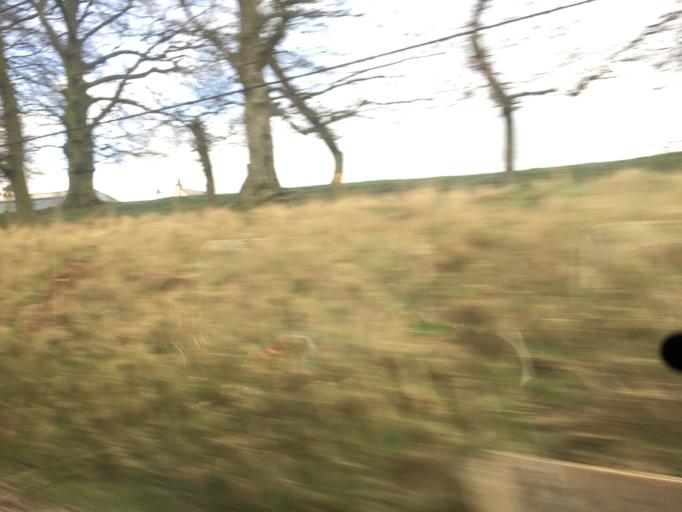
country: GB
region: Scotland
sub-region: Dumfries and Galloway
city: Moffat
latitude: 55.2775
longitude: -3.4205
